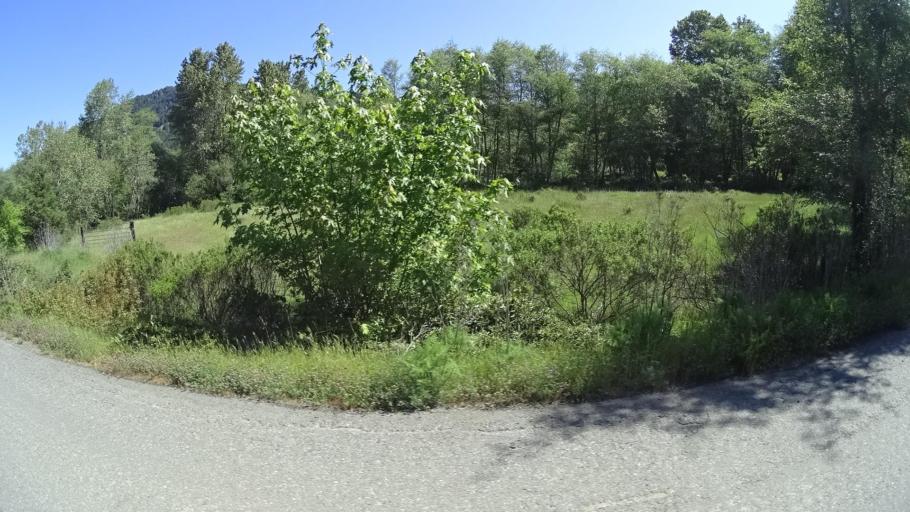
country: US
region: California
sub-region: Humboldt County
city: Rio Dell
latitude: 40.2355
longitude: -124.1180
